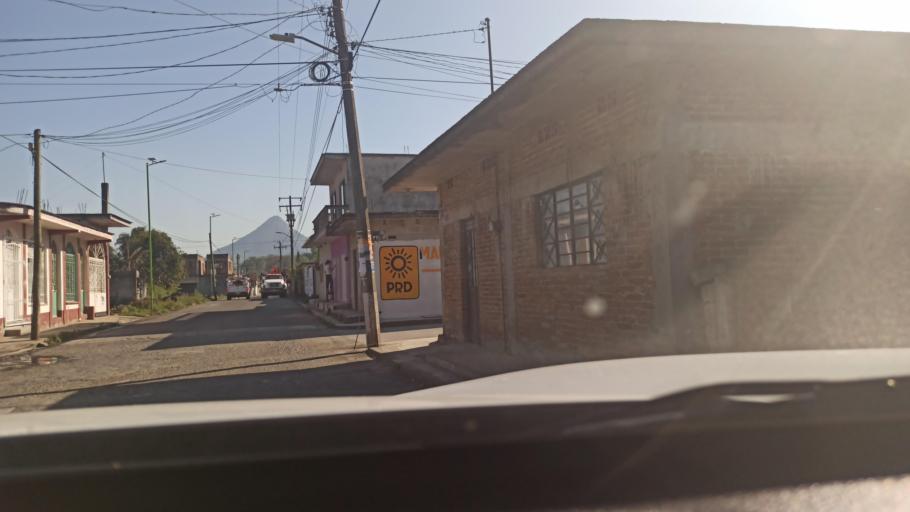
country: MX
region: Veracruz
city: Atzacan
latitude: 18.9109
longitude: -97.0858
